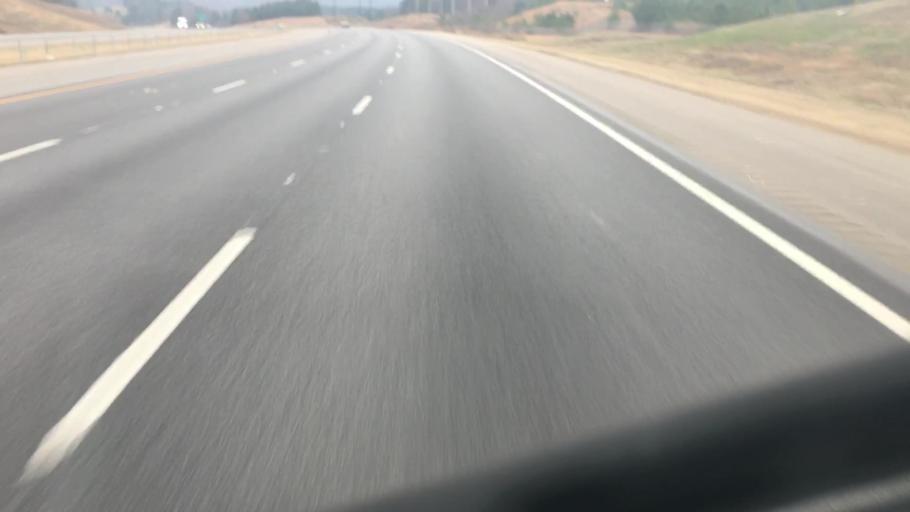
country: US
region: Alabama
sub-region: Jefferson County
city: Fultondale
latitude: 33.5848
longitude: -86.8306
